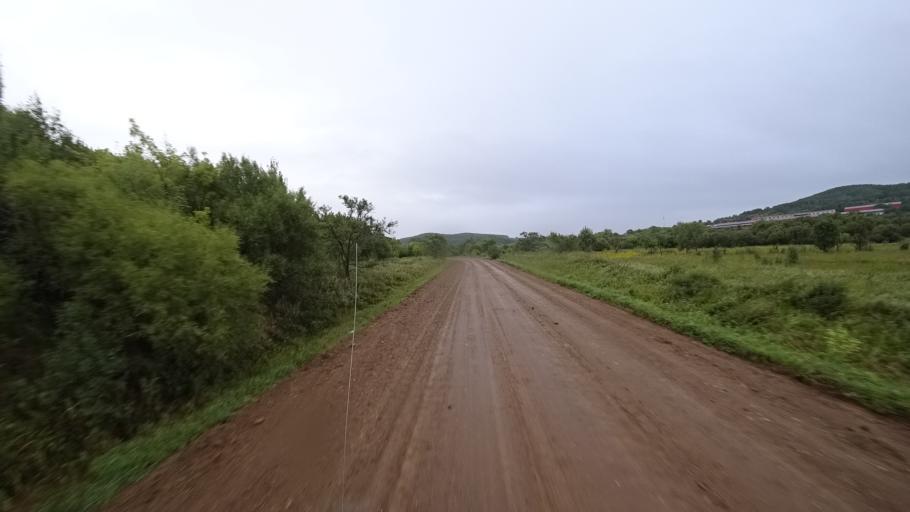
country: RU
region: Primorskiy
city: Monastyrishche
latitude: 44.2736
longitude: 132.4614
